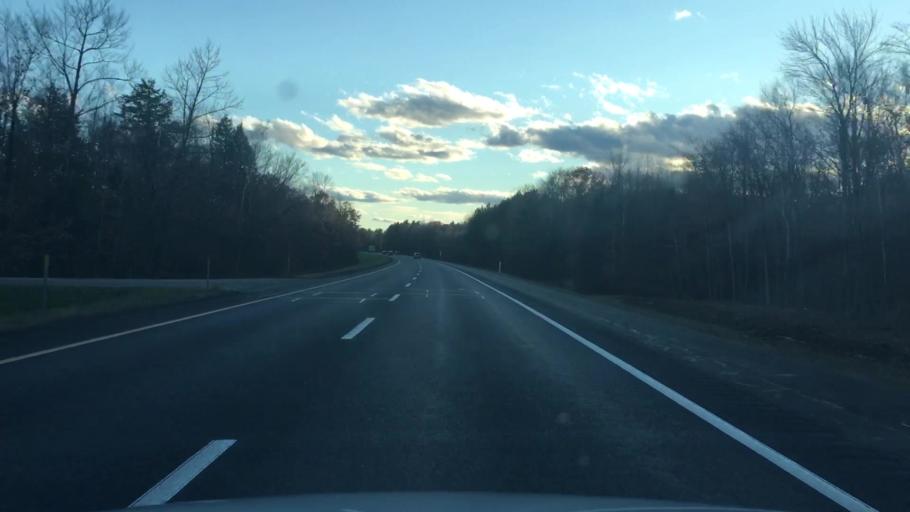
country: US
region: Maine
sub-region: Kennebec County
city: Oakland
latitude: 44.5189
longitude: -69.7007
